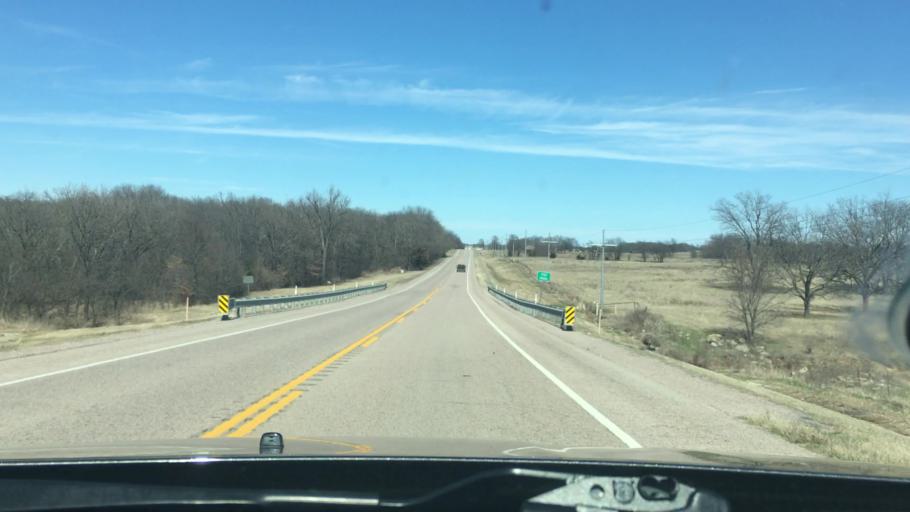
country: US
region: Oklahoma
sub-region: Murray County
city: Sulphur
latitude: 34.4087
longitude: -96.9508
